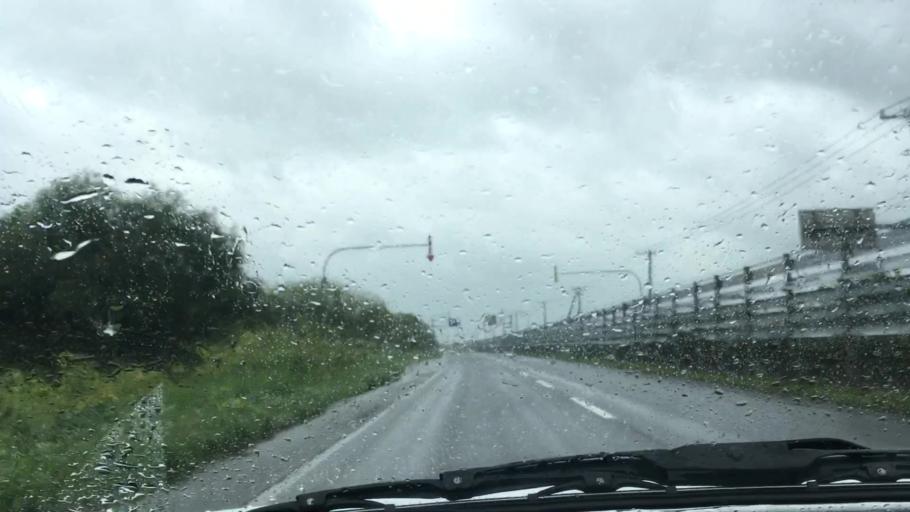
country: JP
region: Hokkaido
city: Nanae
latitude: 42.3066
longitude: 140.2724
